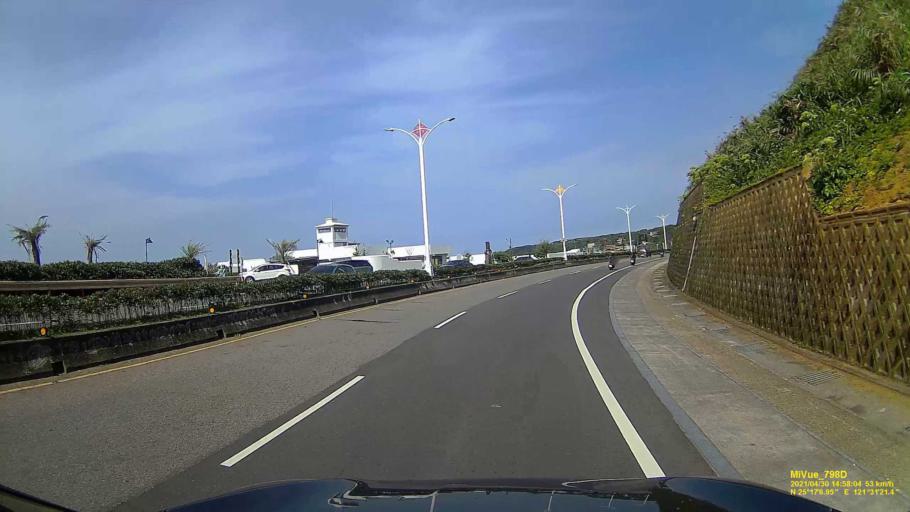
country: TW
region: Taipei
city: Taipei
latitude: 25.2854
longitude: 121.5229
